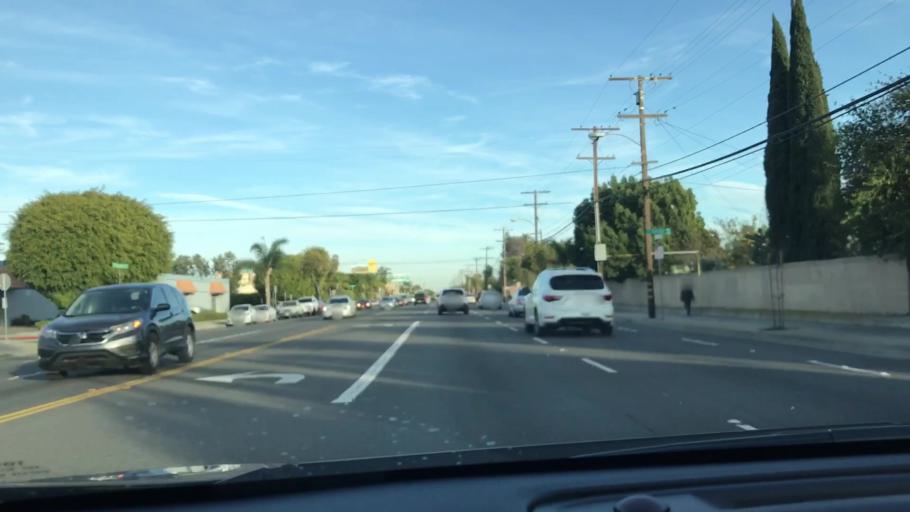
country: US
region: California
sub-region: Los Angeles County
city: Alondra Park
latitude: 33.9019
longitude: -118.3389
